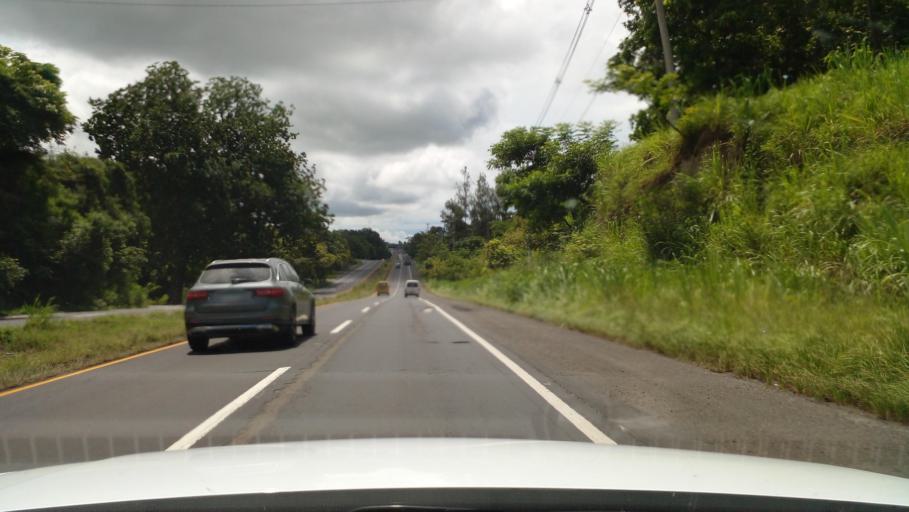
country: PA
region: Panama
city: Las Colinas
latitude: 8.4424
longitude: -80.0455
